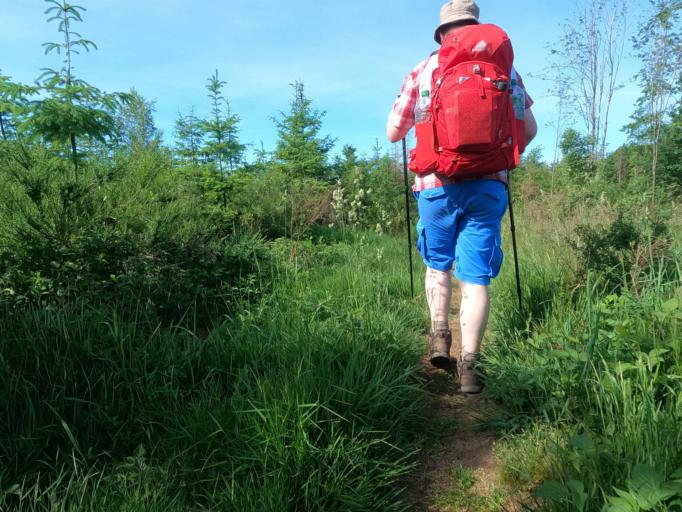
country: DE
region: Rheinland-Pfalz
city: Bolsberg
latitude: 50.6591
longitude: 7.9212
